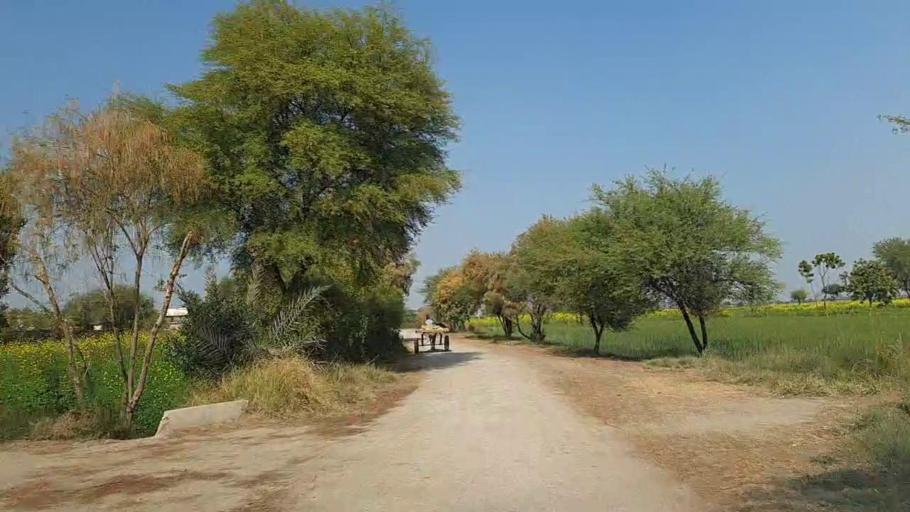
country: PK
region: Sindh
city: Nawabshah
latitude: 26.2906
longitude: 68.5138
